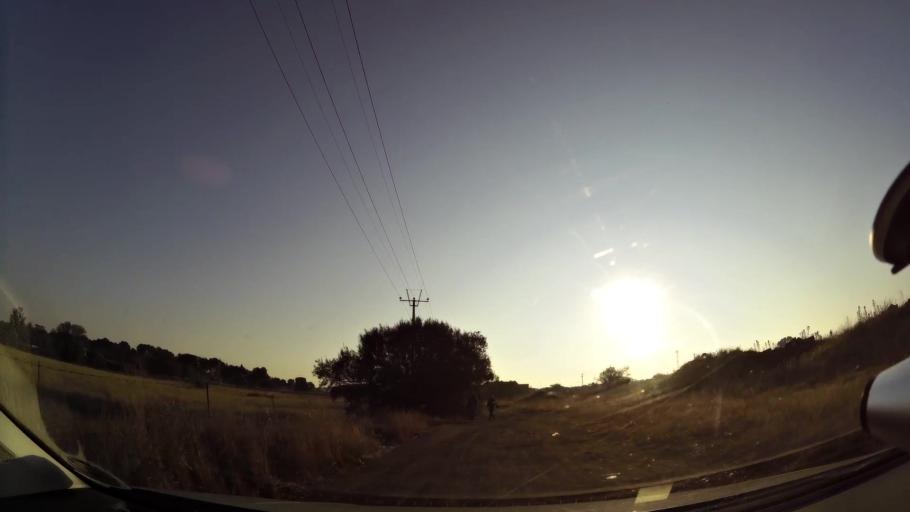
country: ZA
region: Orange Free State
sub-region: Mangaung Metropolitan Municipality
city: Bloemfontein
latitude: -29.0787
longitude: 26.1498
